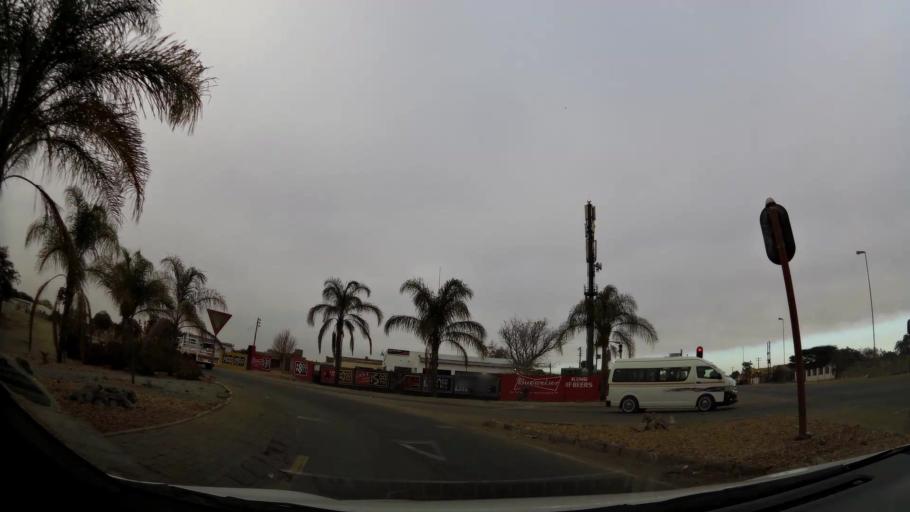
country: ZA
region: Limpopo
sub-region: Capricorn District Municipality
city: Polokwane
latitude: -23.8339
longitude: 29.3794
